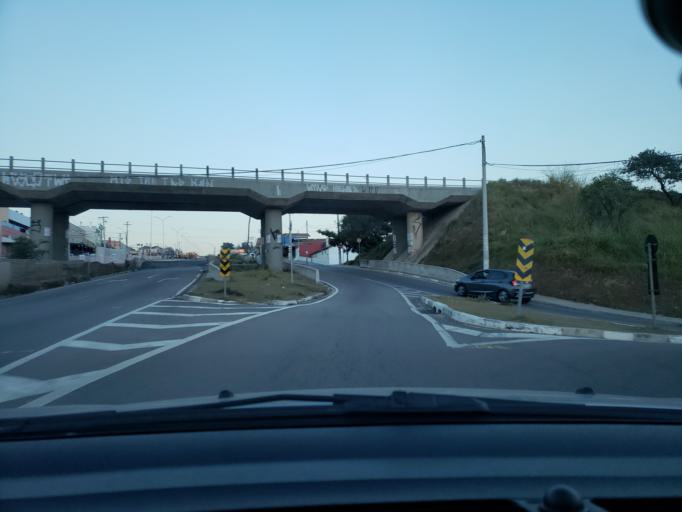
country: BR
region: Sao Paulo
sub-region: Hortolandia
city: Hortolandia
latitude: -22.9369
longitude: -47.1603
